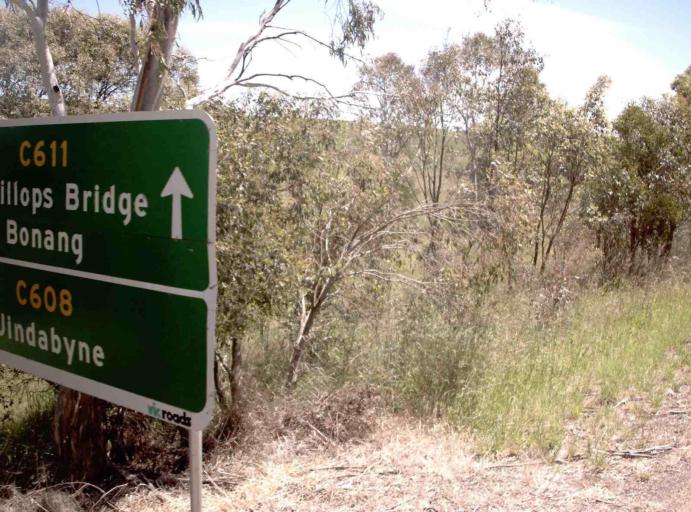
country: AU
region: New South Wales
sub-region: Snowy River
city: Jindabyne
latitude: -37.1015
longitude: 148.2515
